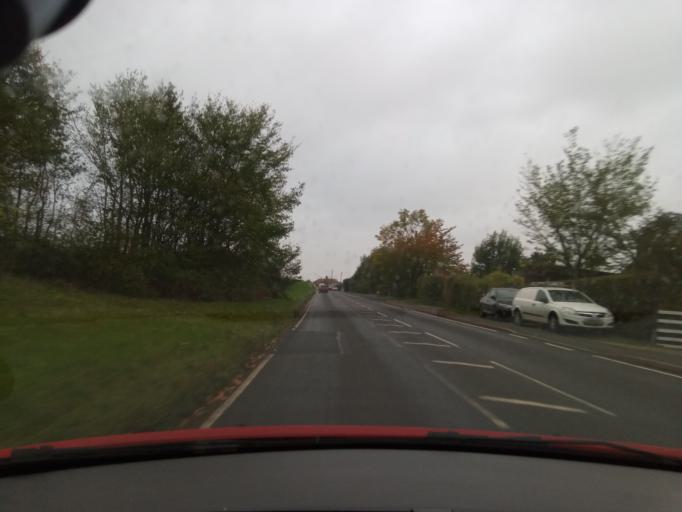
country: GB
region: England
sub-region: Suffolk
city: Kedington
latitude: 52.0641
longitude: 0.4847
